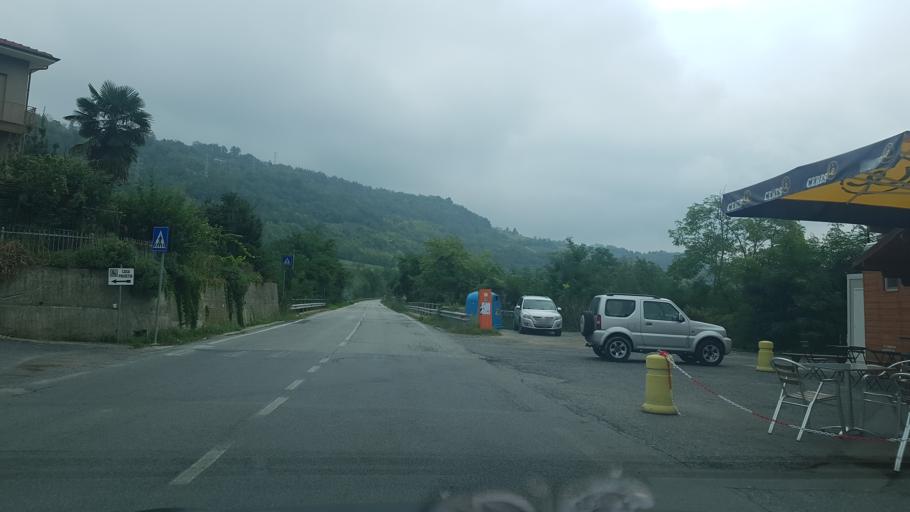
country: IT
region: Piedmont
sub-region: Provincia di Cuneo
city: Bastia Mondovi
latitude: 44.4411
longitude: 7.8949
